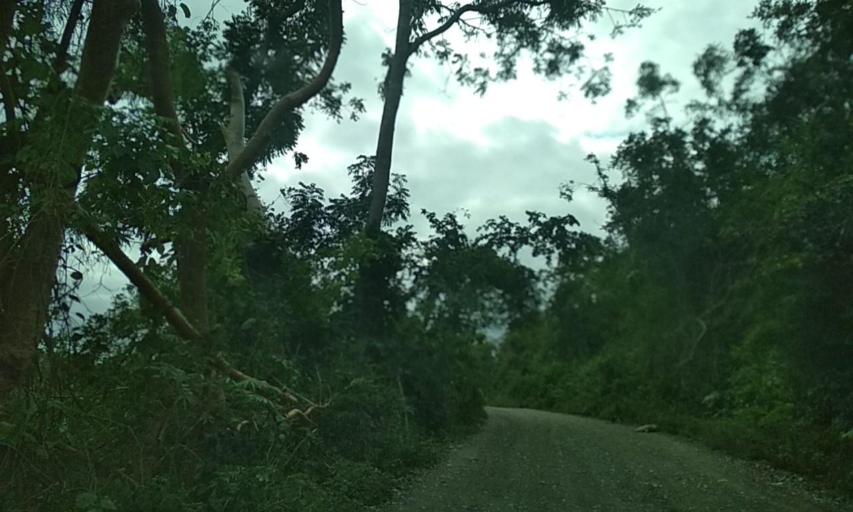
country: MX
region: Veracruz
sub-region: Papantla
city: Residencial Tajin
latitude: 20.6207
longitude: -97.3615
